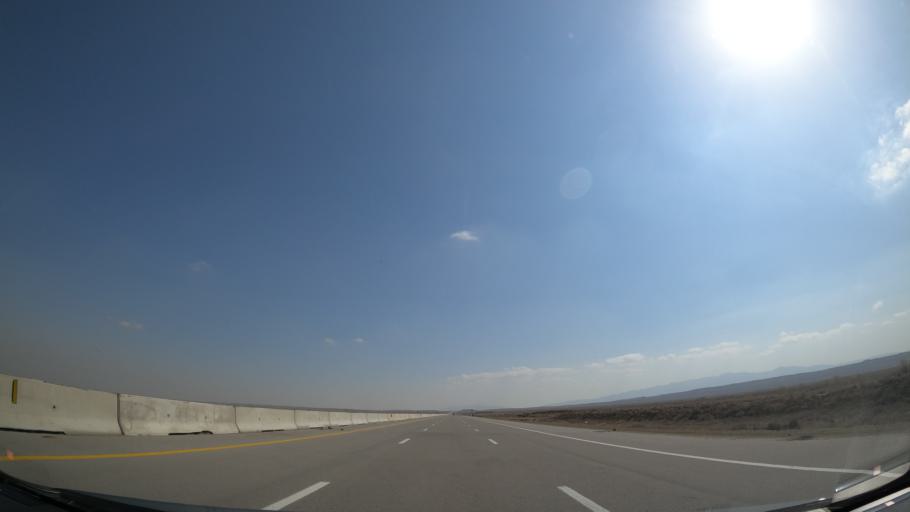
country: IR
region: Alborz
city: Nazarabad
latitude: 35.8253
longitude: 50.5070
